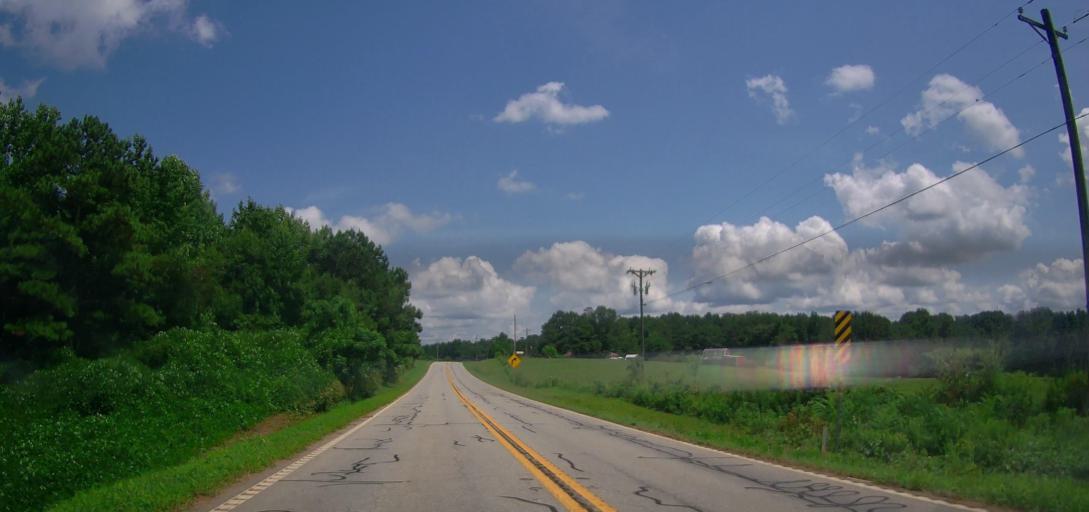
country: US
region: Georgia
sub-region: Carroll County
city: Bowdon
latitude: 33.4146
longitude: -85.2589
